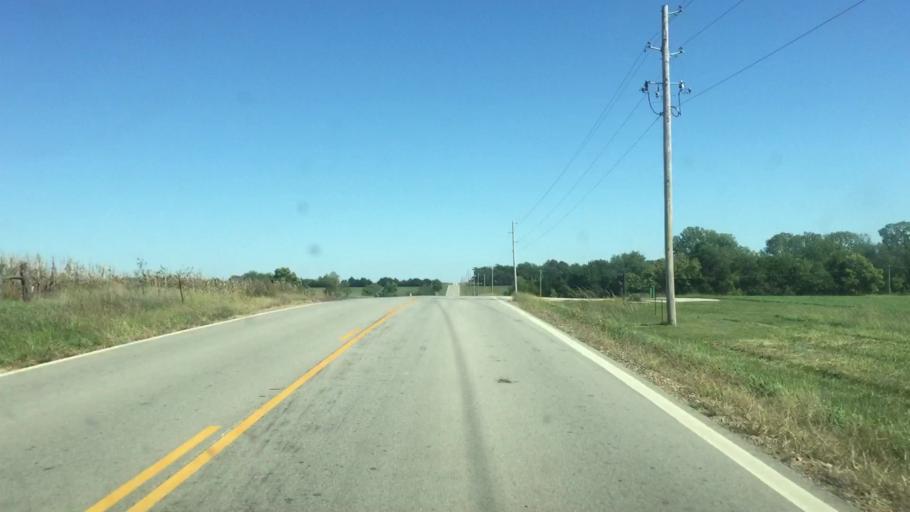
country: US
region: Kansas
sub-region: Jackson County
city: Holton
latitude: 39.5949
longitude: -95.7074
